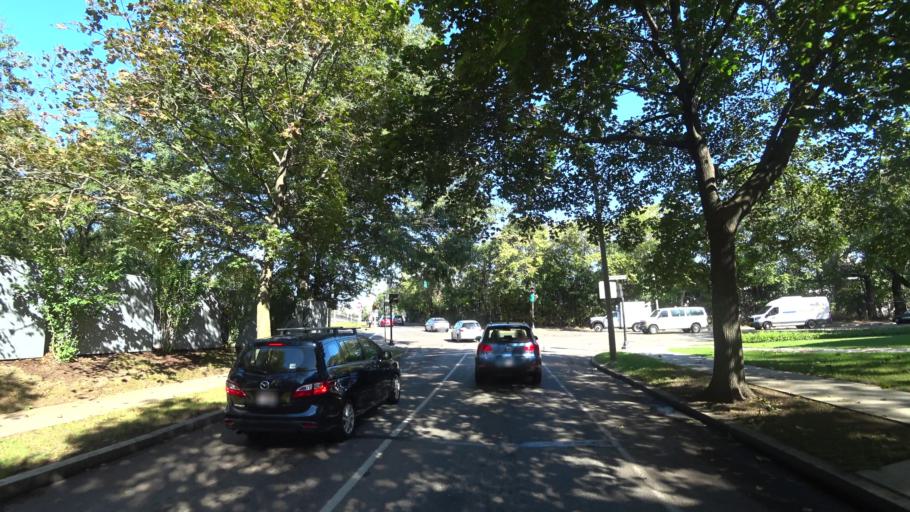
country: US
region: Massachusetts
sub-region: Norfolk County
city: Brookline
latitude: 42.3485
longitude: -71.1091
